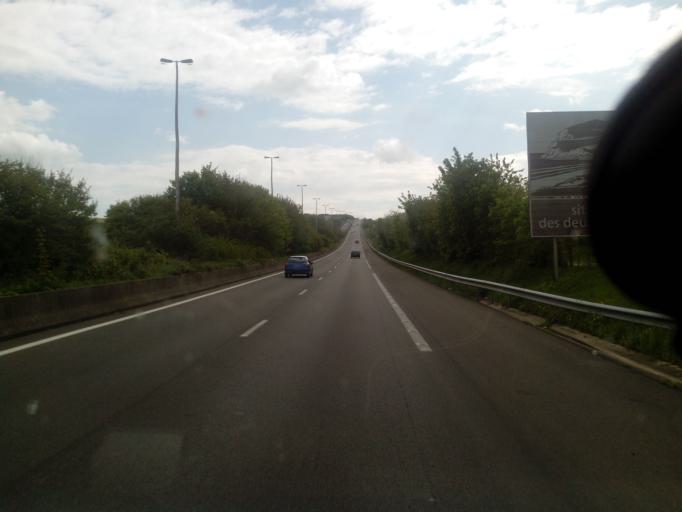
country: FR
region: Nord-Pas-de-Calais
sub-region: Departement du Pas-de-Calais
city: Sangatte
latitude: 50.8935
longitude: 1.7613
